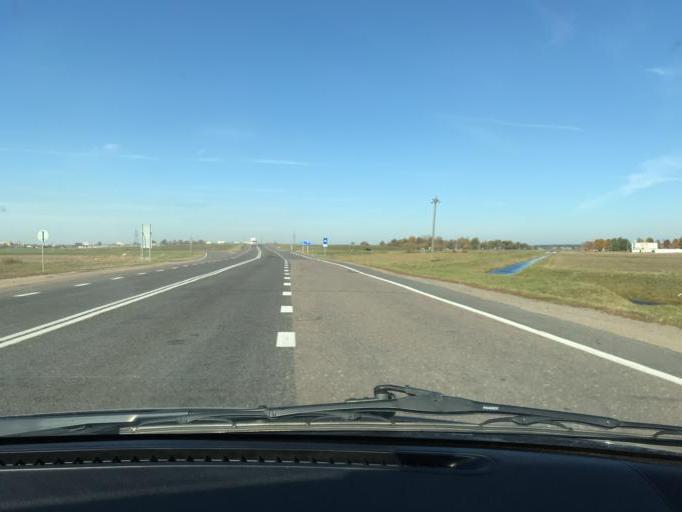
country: BY
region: Brest
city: Ivatsevichy
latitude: 52.6946
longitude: 25.3651
